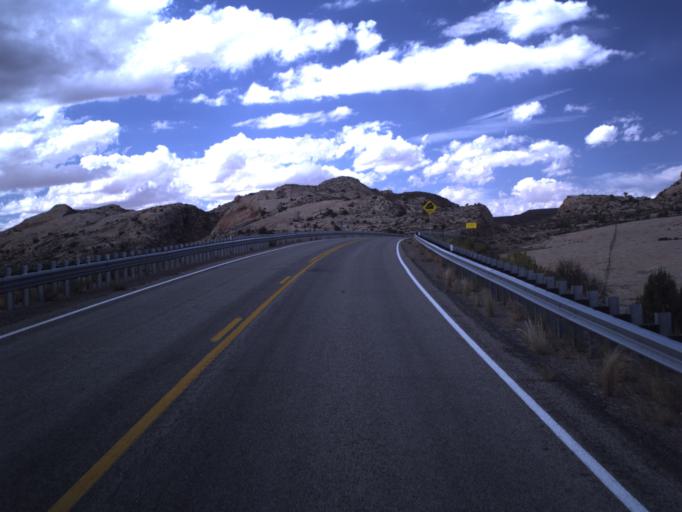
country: US
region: Utah
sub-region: San Juan County
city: Blanding
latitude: 37.2599
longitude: -109.6670
